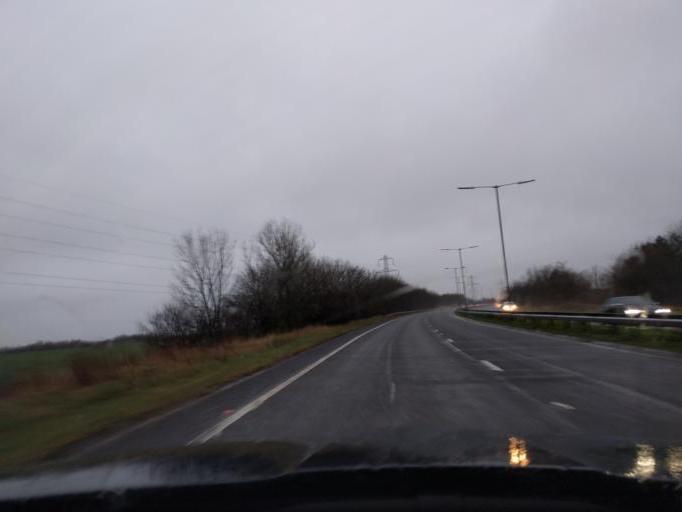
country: GB
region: England
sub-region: Northumberland
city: Newbiggin-by-the-Sea
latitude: 55.1785
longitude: -1.5314
